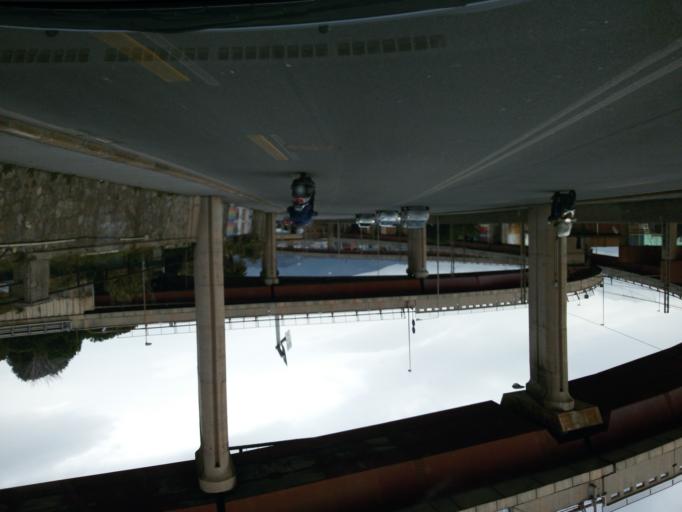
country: IT
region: Liguria
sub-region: Provincia di Genova
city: San Teodoro
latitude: 44.4158
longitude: 8.8613
